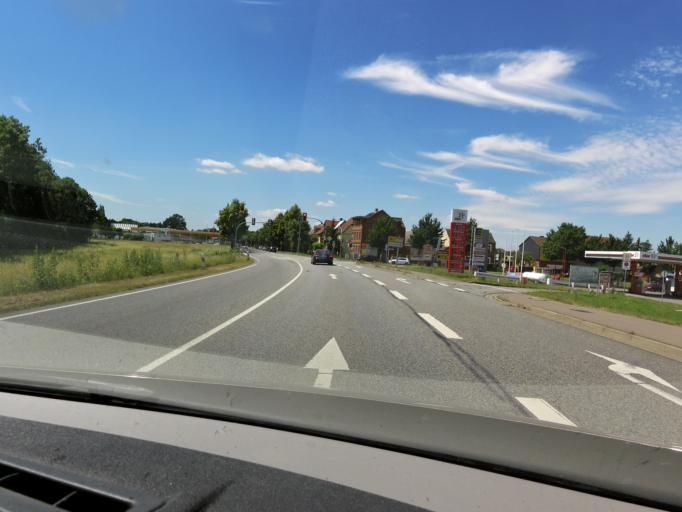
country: DE
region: Saxony-Anhalt
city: Merseburg
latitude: 51.3598
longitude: 12.0201
